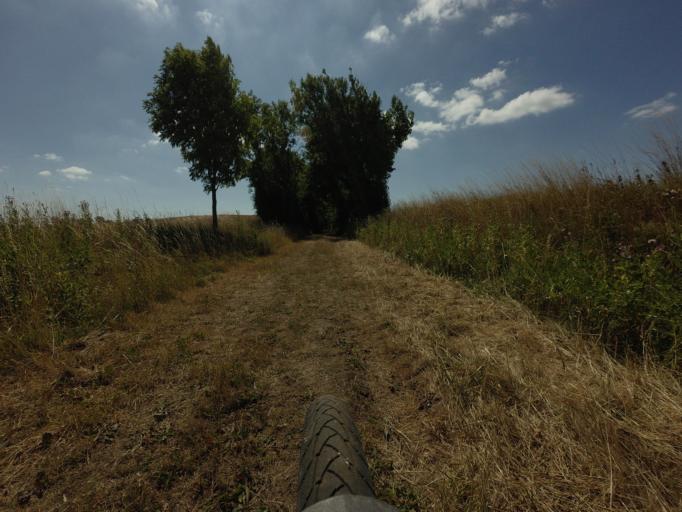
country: DK
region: Central Jutland
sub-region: Odder Kommune
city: Odder
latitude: 55.9183
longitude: 10.1103
